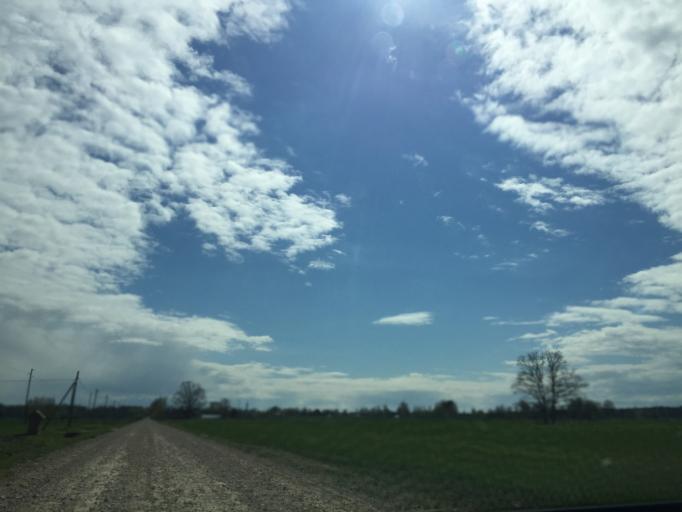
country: LV
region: Jelgava
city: Jelgava
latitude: 56.5700
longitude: 23.7832
